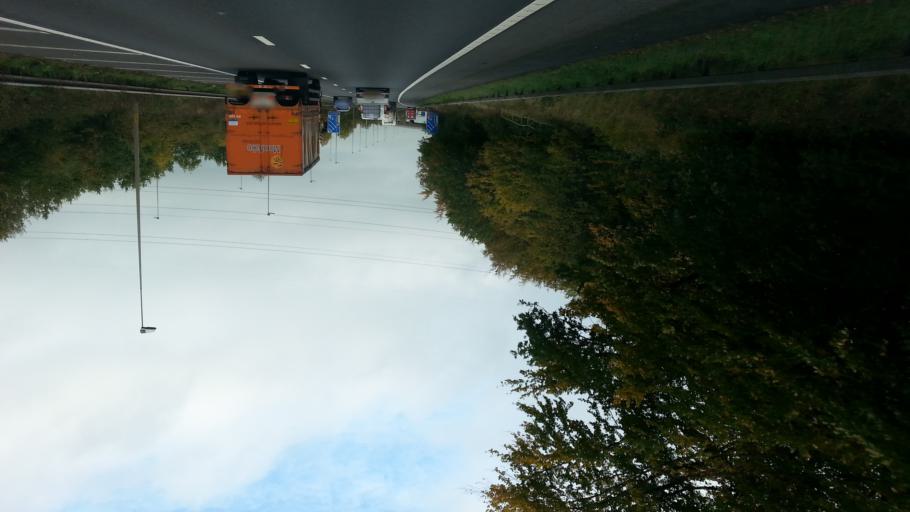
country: GB
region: England
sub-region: Staffordshire
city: Featherstone
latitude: 52.6671
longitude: -2.0709
